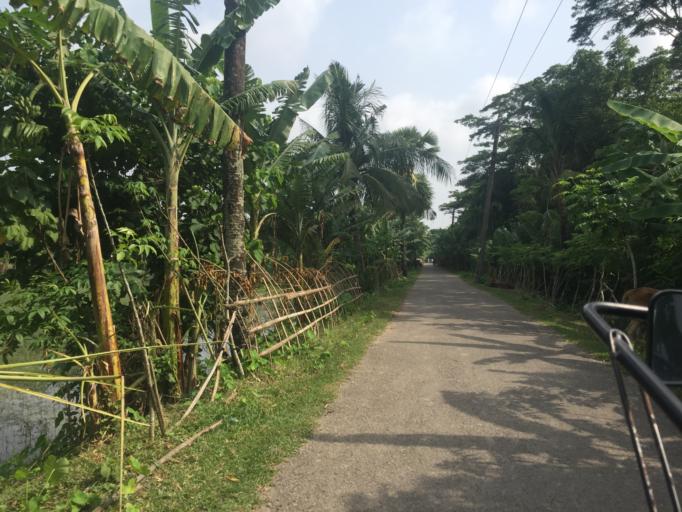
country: BD
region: Barisal
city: Mathba
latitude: 22.2370
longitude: 89.9152
